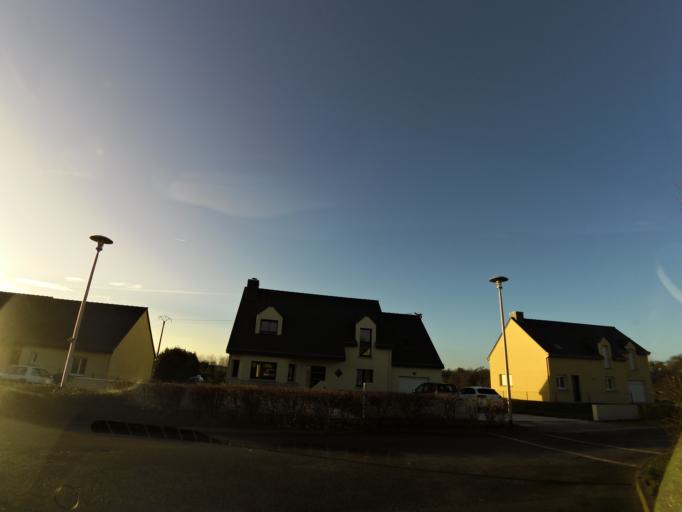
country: FR
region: Brittany
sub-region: Departement d'Ille-et-Vilaine
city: Pance
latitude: 47.8986
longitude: -1.6095
